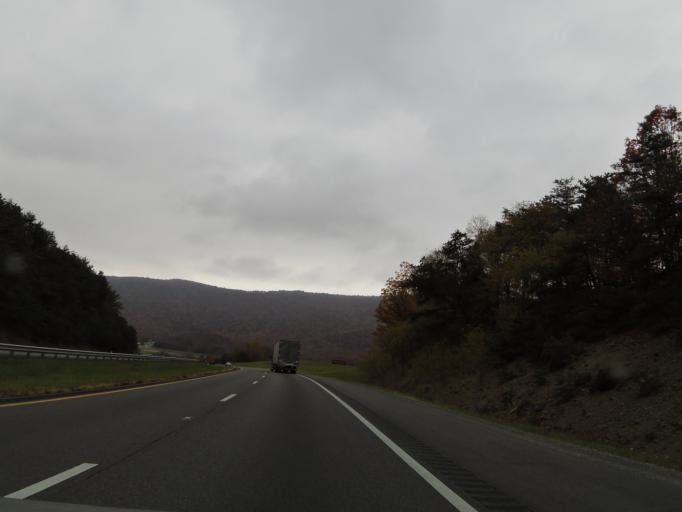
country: US
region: Virginia
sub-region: Bland County
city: Bland
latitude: 37.0271
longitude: -81.1085
